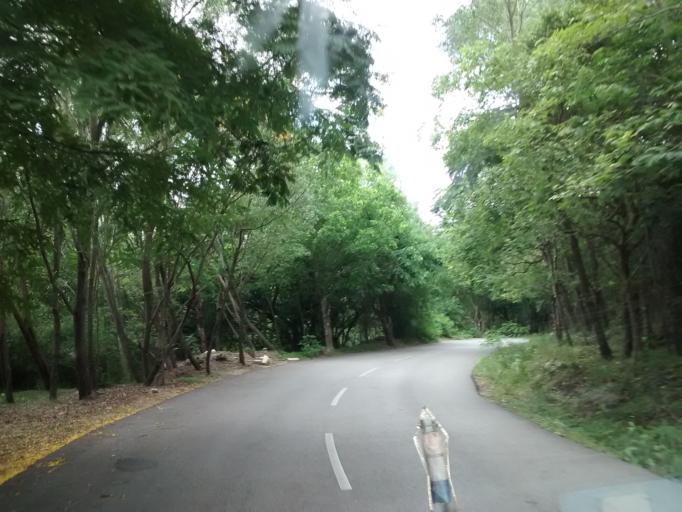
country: IN
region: Andhra Pradesh
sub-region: Chittoor
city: Tirumala
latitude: 13.6826
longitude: 79.3323
